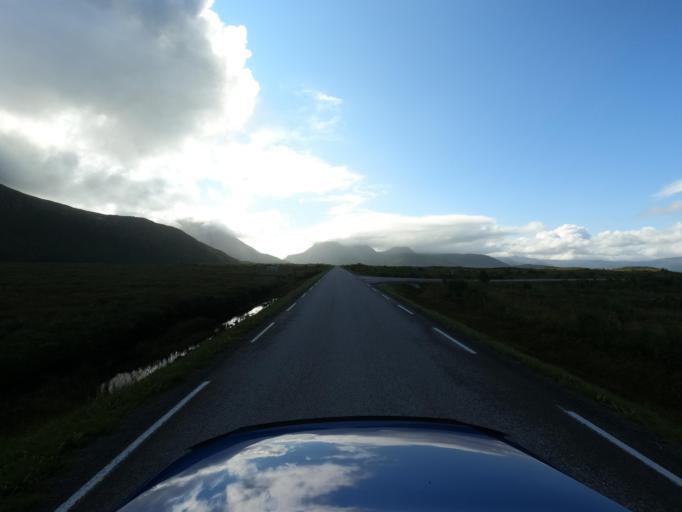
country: NO
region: Nordland
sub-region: Vagan
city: Kabelvag
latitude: 68.3052
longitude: 14.1834
